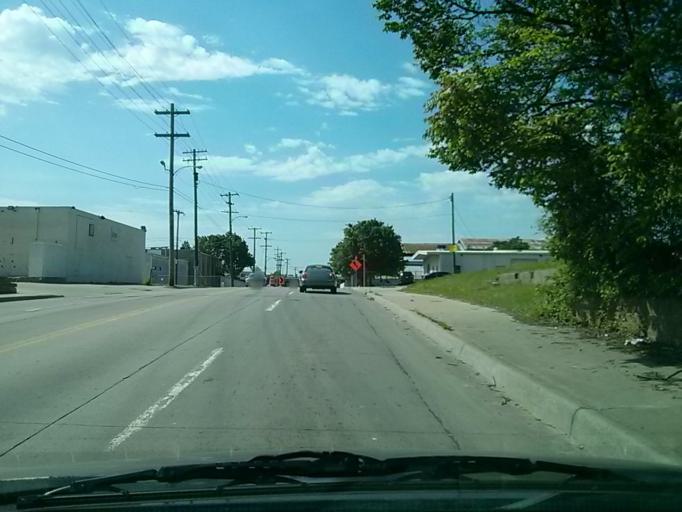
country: US
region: Oklahoma
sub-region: Tulsa County
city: Tulsa
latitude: 36.1619
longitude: -95.9757
